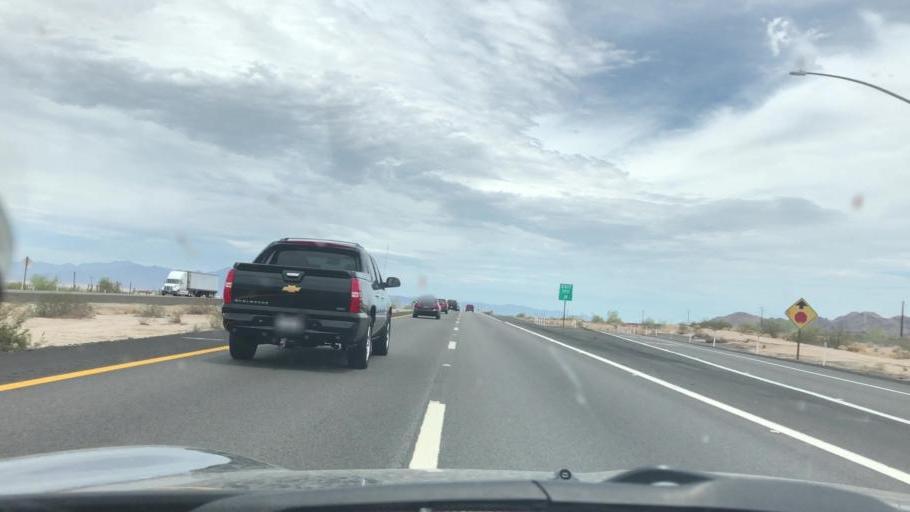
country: US
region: California
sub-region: Imperial County
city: Niland
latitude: 33.7103
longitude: -115.4036
